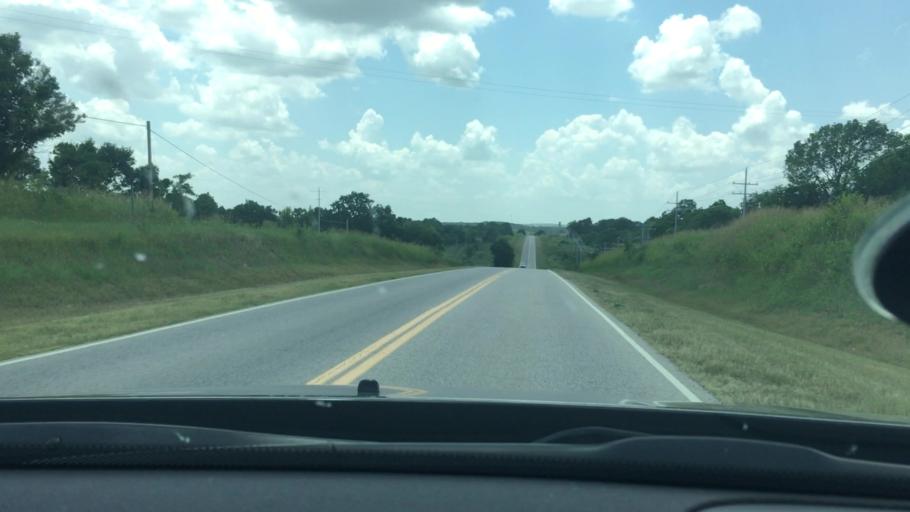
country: US
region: Oklahoma
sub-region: Pontotoc County
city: Ada
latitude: 34.6310
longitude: -96.6348
